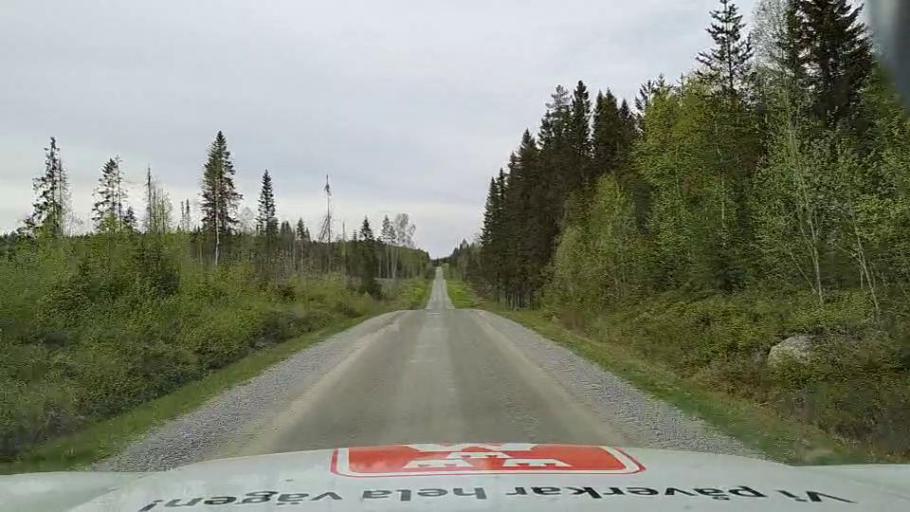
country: SE
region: Jaemtland
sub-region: OEstersunds Kommun
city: Brunflo
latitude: 62.6238
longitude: 14.9435
